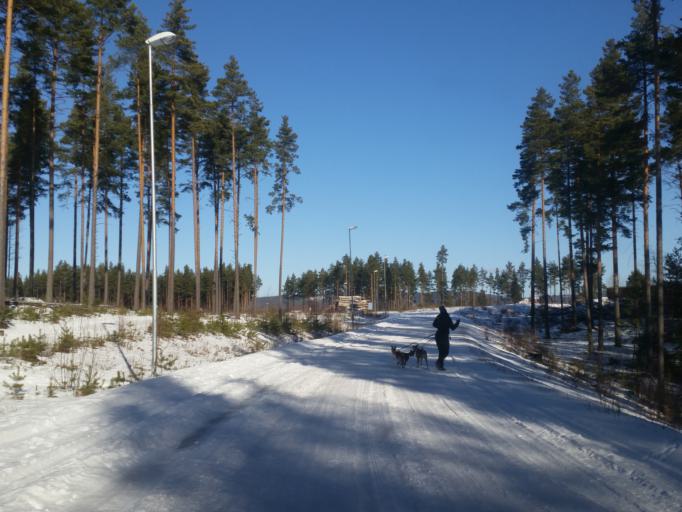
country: SE
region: Dalarna
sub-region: Leksand Municipality
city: Smedby
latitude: 60.6707
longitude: 15.0851
